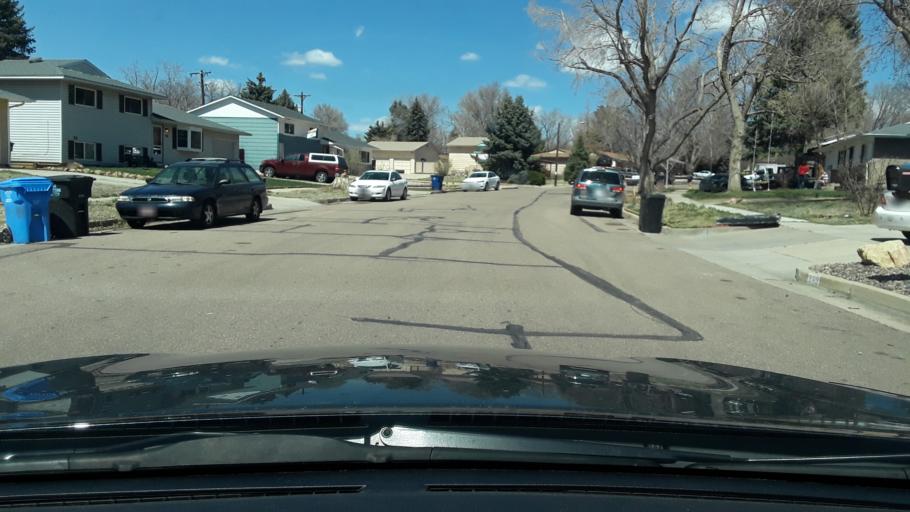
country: US
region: Colorado
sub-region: El Paso County
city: Colorado Springs
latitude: 38.8451
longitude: -104.7682
